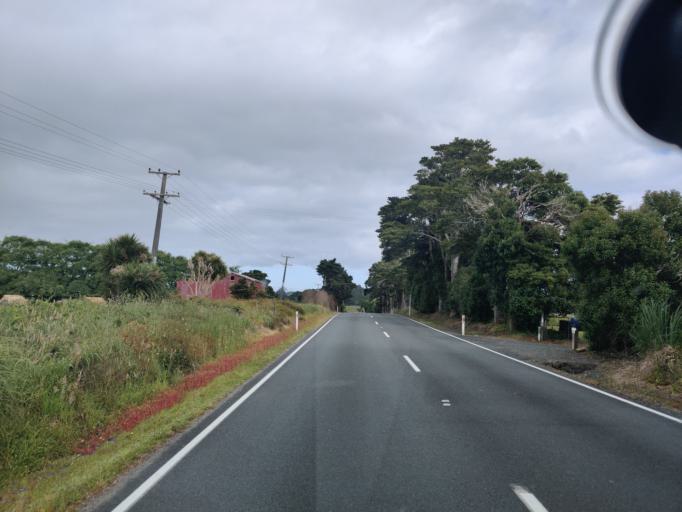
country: NZ
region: Northland
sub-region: Whangarei
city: Ngunguru
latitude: -35.5673
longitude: 174.3963
